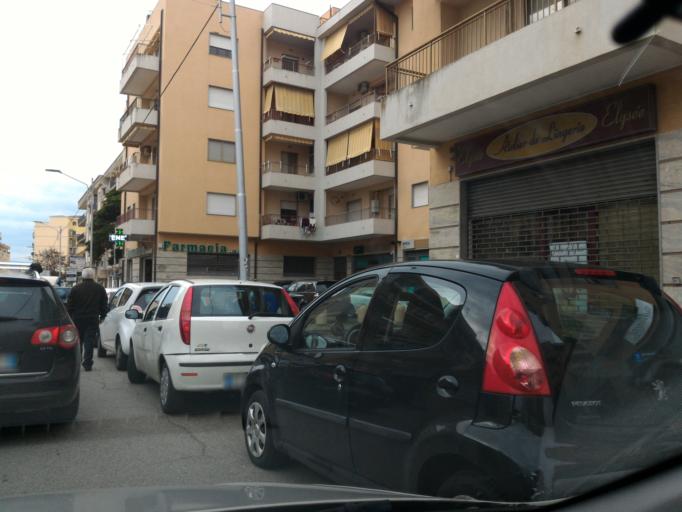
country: IT
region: Calabria
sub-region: Provincia di Catanzaro
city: Roccelletta
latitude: 38.8253
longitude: 16.6206
